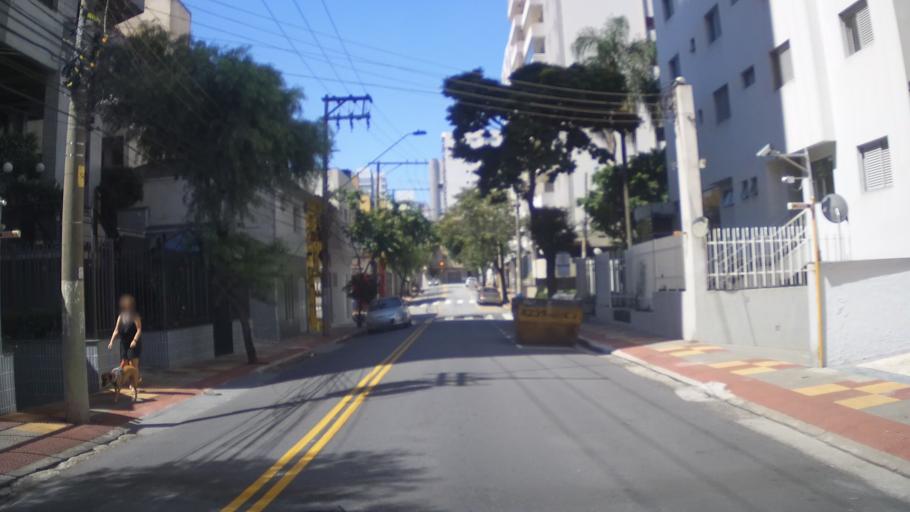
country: BR
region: Sao Paulo
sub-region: Sao Caetano Do Sul
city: Sao Caetano do Sul
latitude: -23.6181
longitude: -46.5711
